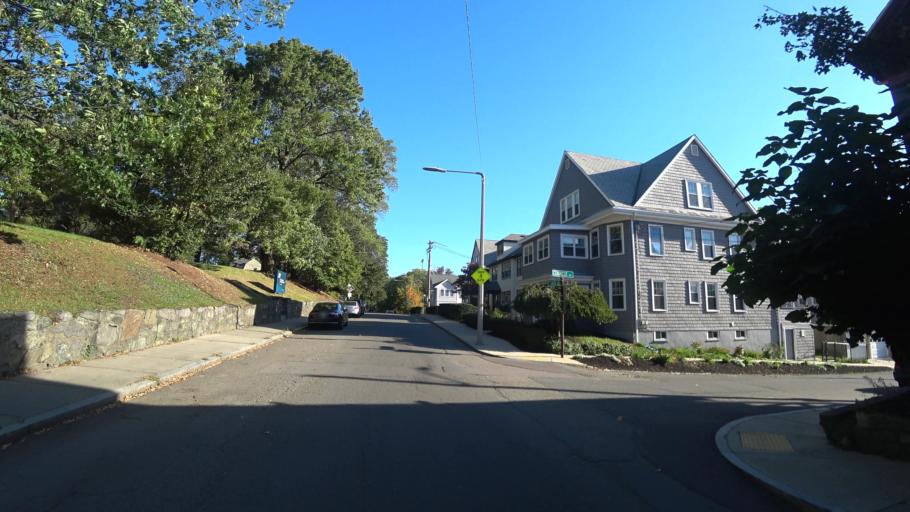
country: US
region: Massachusetts
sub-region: Middlesex County
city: Watertown
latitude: 42.3464
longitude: -71.1621
